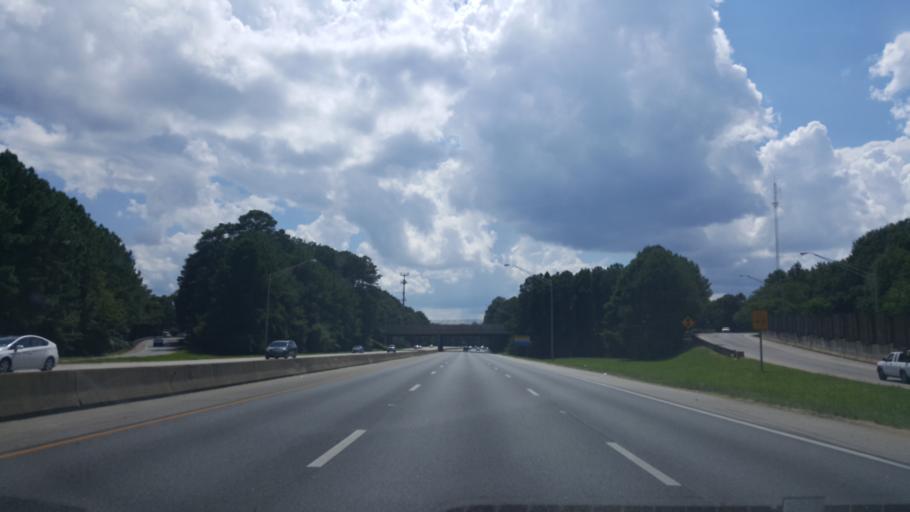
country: US
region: Virginia
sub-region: City of Hampton
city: Hampton
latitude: 37.0177
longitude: -76.3846
